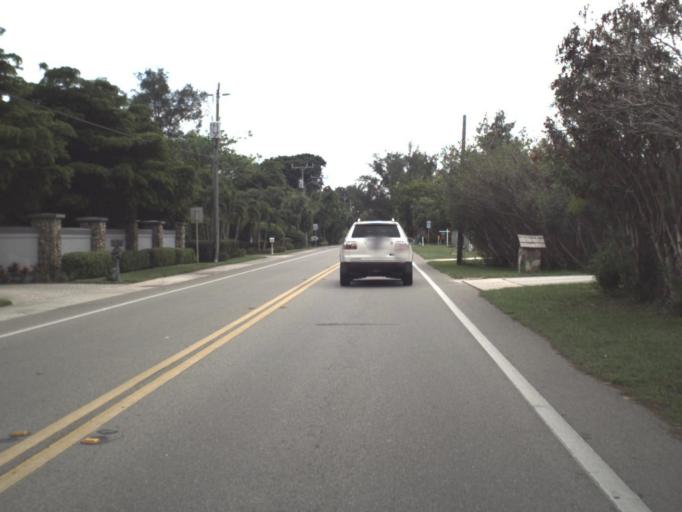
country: US
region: Florida
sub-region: Sarasota County
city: Siesta Key
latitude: 27.2940
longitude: -82.5587
